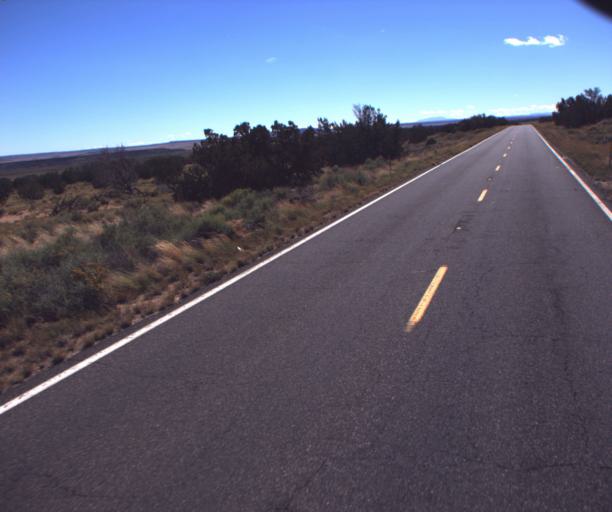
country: US
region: Arizona
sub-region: Apache County
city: Saint Johns
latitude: 34.7882
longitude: -109.2383
